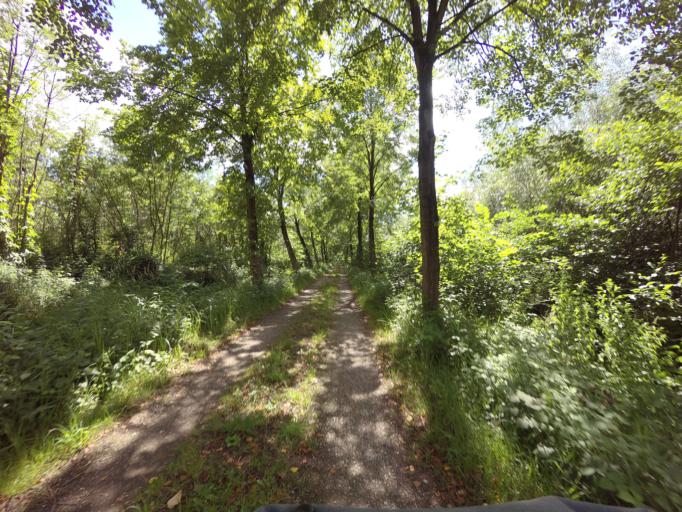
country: NL
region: Utrecht
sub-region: Gemeente Utrechtse Heuvelrug
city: Driebergen-Rijsenburg
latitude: 52.0093
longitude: 5.3014
